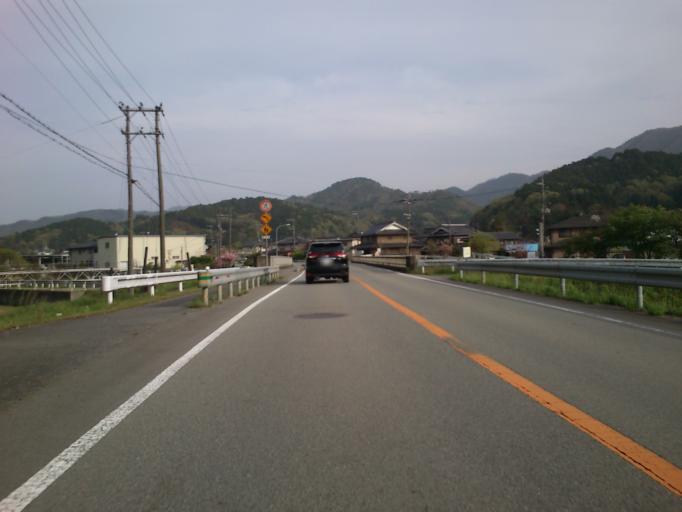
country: JP
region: Hyogo
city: Sasayama
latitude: 35.0817
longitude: 135.3219
